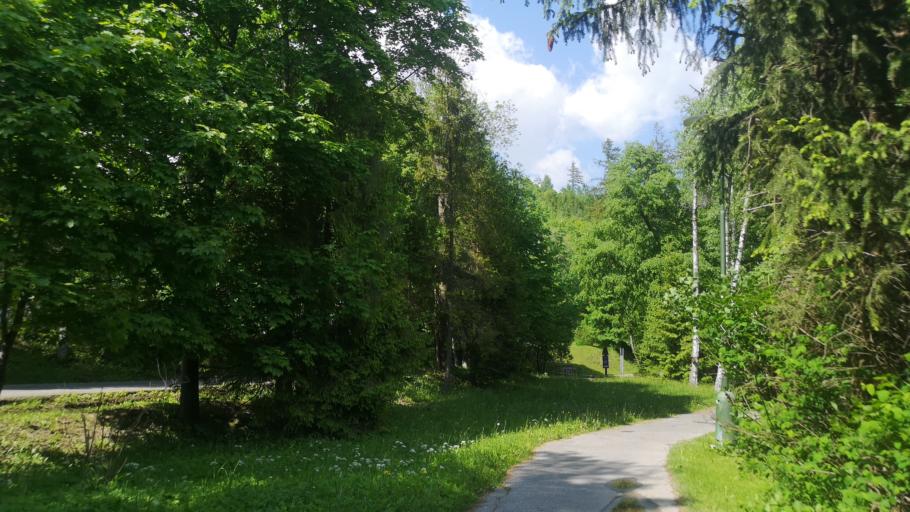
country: SK
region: Presovsky
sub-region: Okres Poprad
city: Vysoke Tatry
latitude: 49.1684
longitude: 20.2735
